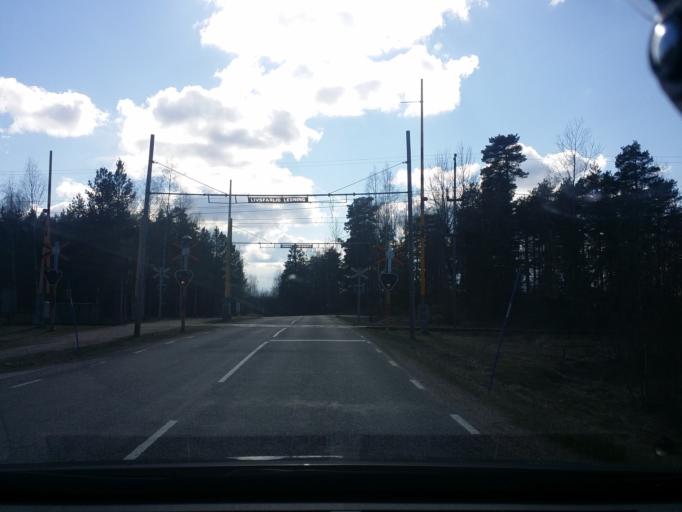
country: SE
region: Vaestmanland
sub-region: Sala Kommun
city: Sala
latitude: 59.9906
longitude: 16.4792
